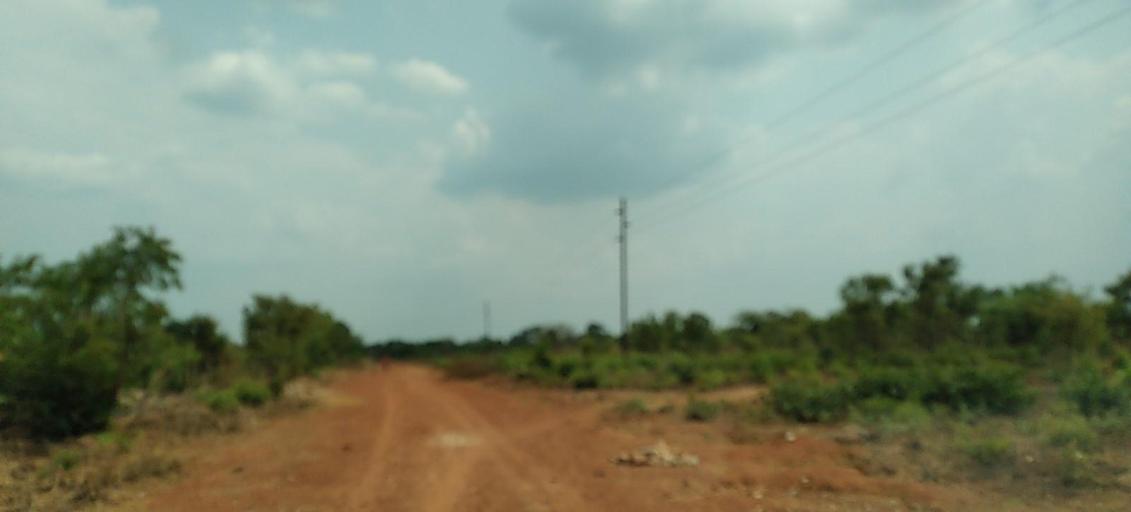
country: ZM
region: Copperbelt
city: Kalulushi
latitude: -12.8883
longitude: 28.0748
